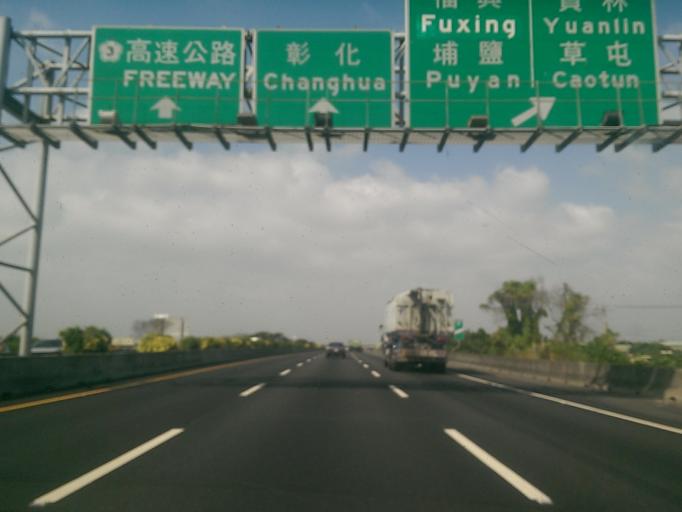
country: TW
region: Taiwan
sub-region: Changhua
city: Chang-hua
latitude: 23.9742
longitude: 120.5063
